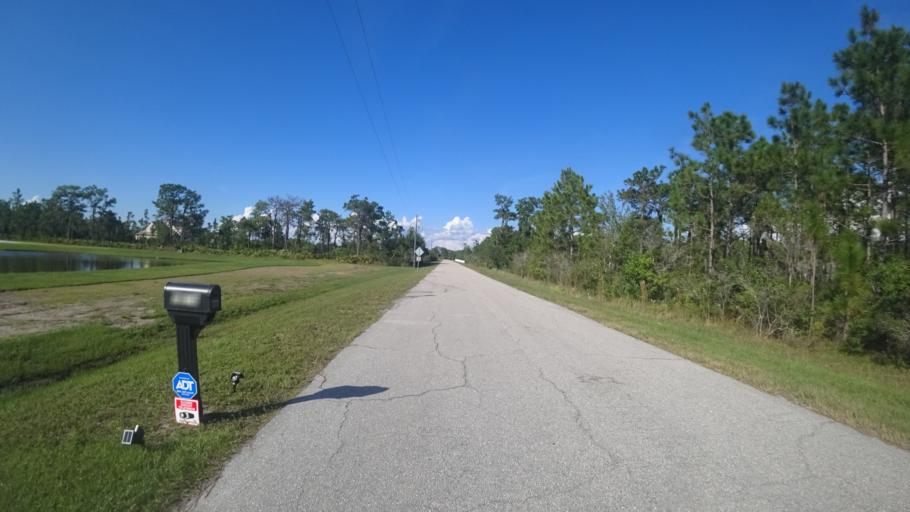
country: US
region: Florida
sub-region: Sarasota County
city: Lake Sarasota
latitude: 27.3980
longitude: -82.2855
